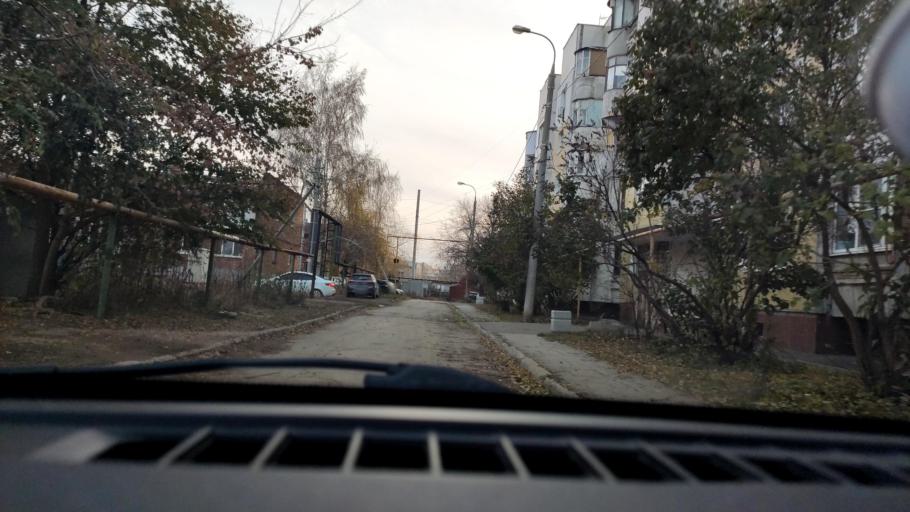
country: RU
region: Samara
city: Samara
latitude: 53.1485
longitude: 50.1386
